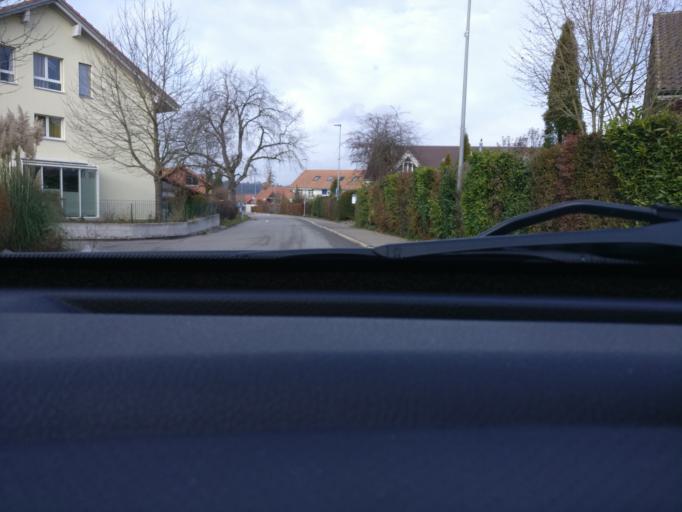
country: CH
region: Bern
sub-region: Bern-Mittelland District
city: Urtenen
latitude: 47.0110
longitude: 7.4839
